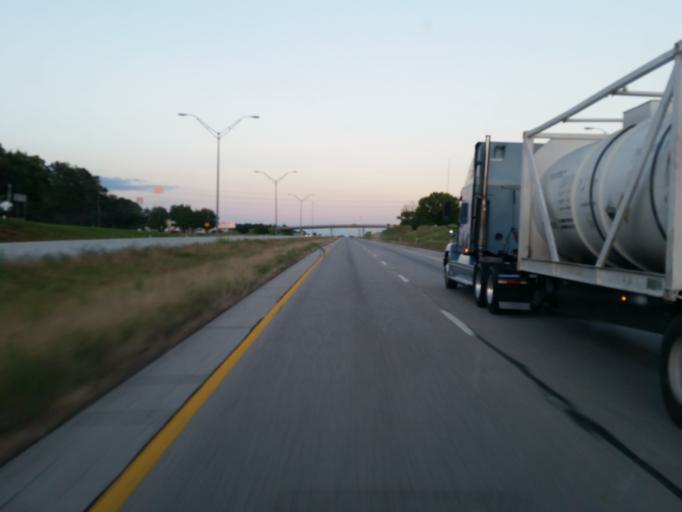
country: US
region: Texas
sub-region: Smith County
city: Hideaway
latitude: 32.4701
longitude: -95.4571
